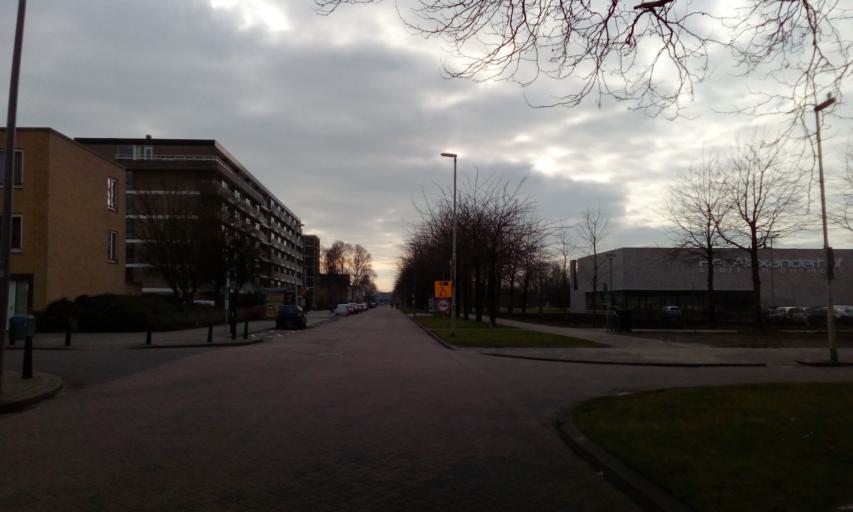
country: NL
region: South Holland
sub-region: Gemeente Rotterdam
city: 's-Gravenland
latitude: 51.9375
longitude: 4.5522
